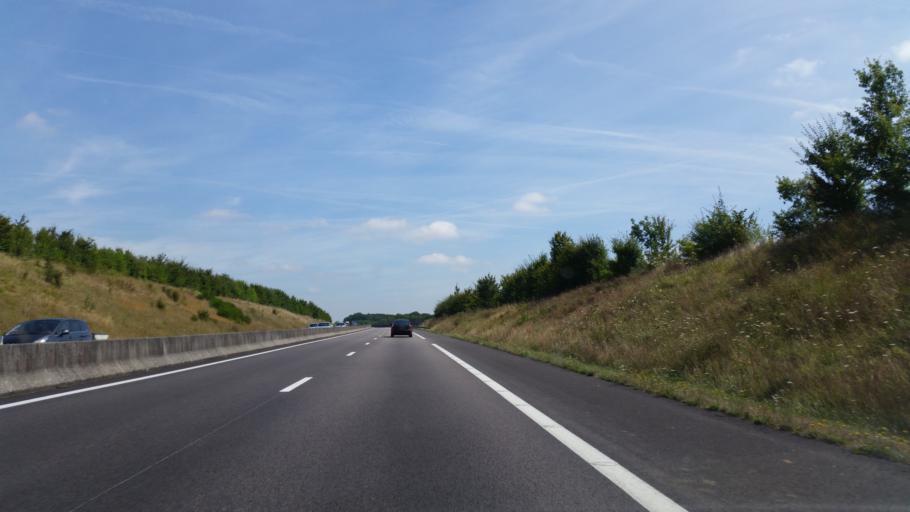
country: FR
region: Haute-Normandie
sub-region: Departement de la Seine-Maritime
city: Aumale
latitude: 49.7443
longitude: 1.6594
